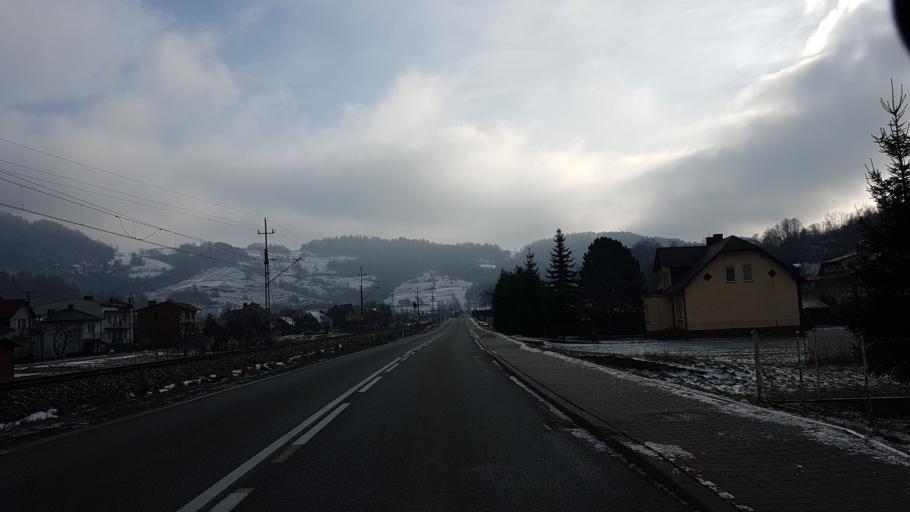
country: PL
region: Lesser Poland Voivodeship
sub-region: Powiat nowosadecki
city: Rytro
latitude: 49.4715
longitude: 20.6910
